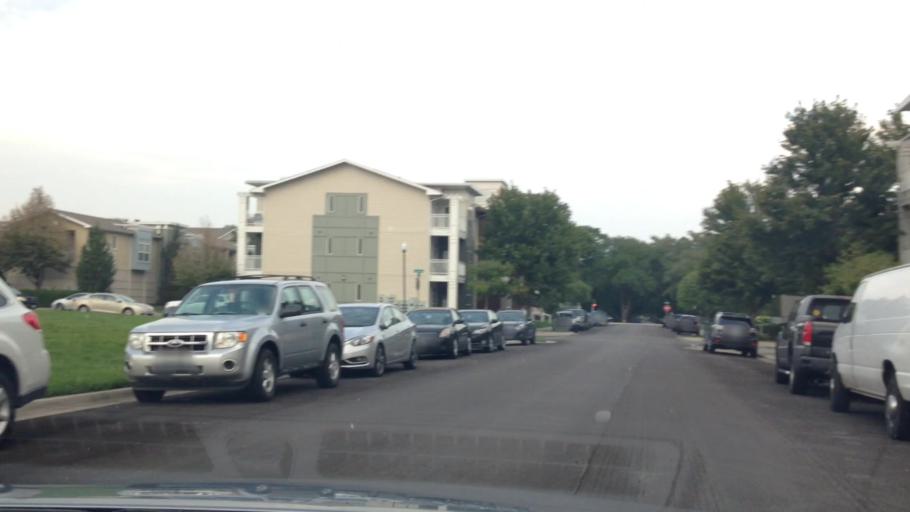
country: US
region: Missouri
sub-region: Clay County
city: North Kansas City
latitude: 39.1485
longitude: -94.5790
